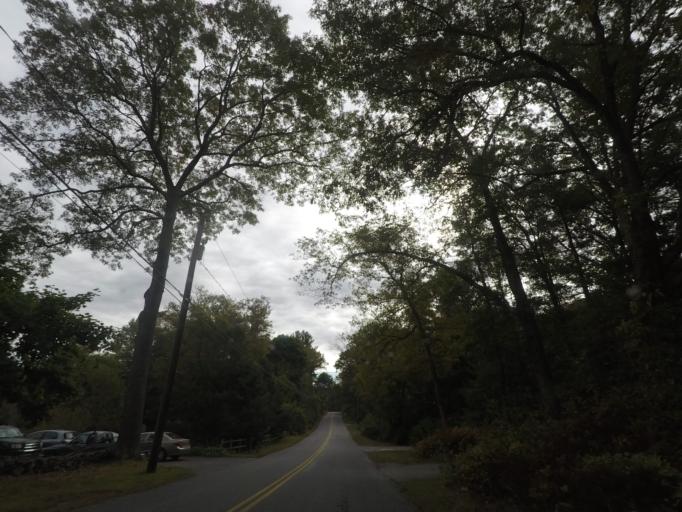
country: US
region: Connecticut
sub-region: Windham County
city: Thompson
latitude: 41.9491
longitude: -71.8401
